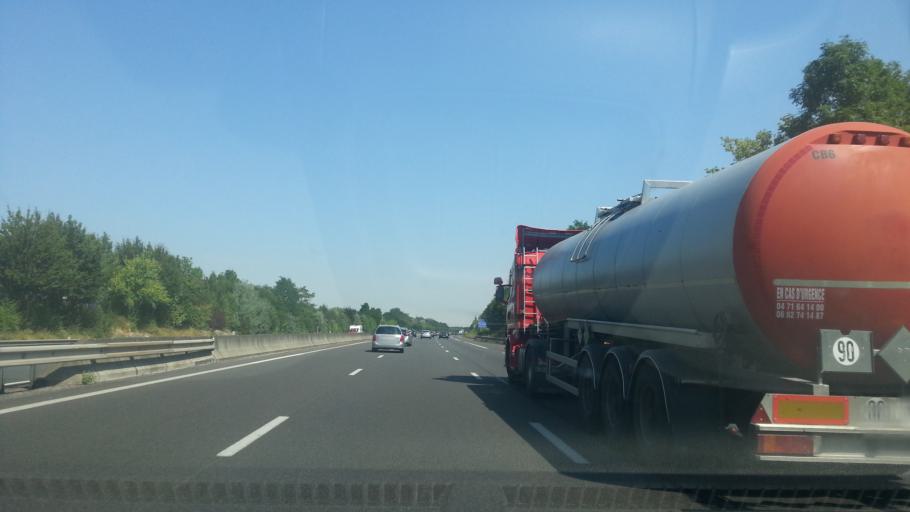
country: FR
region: Centre
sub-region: Departement du Loiret
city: Saran
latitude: 47.9557
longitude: 1.8510
